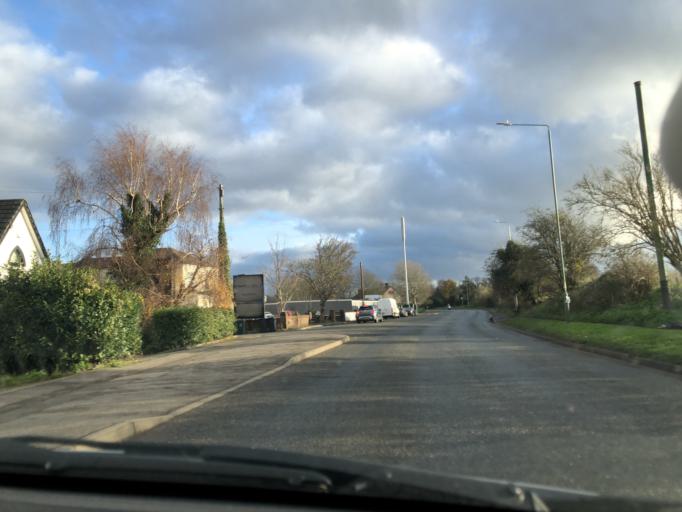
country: GB
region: England
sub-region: Kent
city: Dartford
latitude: 51.4307
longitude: 0.2201
